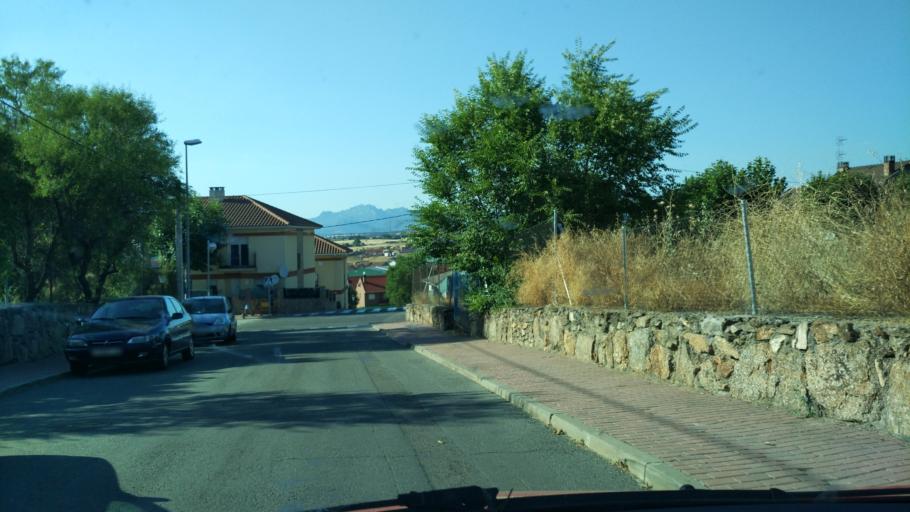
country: ES
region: Madrid
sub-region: Provincia de Madrid
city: Pedrezuela
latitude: 40.7438
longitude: -3.5981
